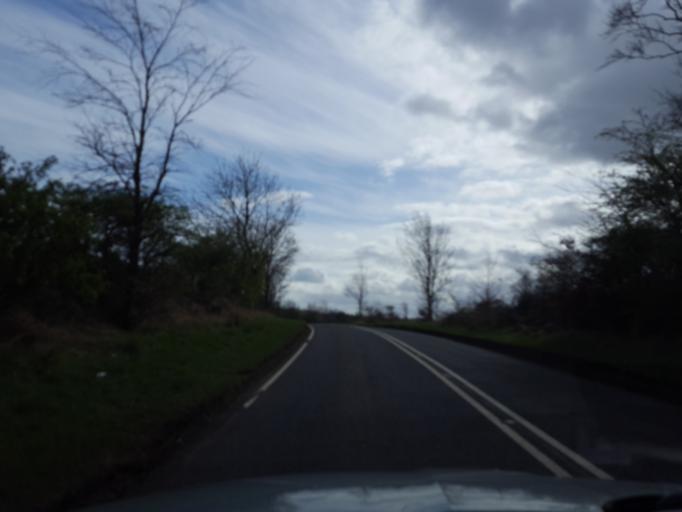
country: GB
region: Scotland
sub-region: West Lothian
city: Bathgate
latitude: 55.9528
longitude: -3.6631
